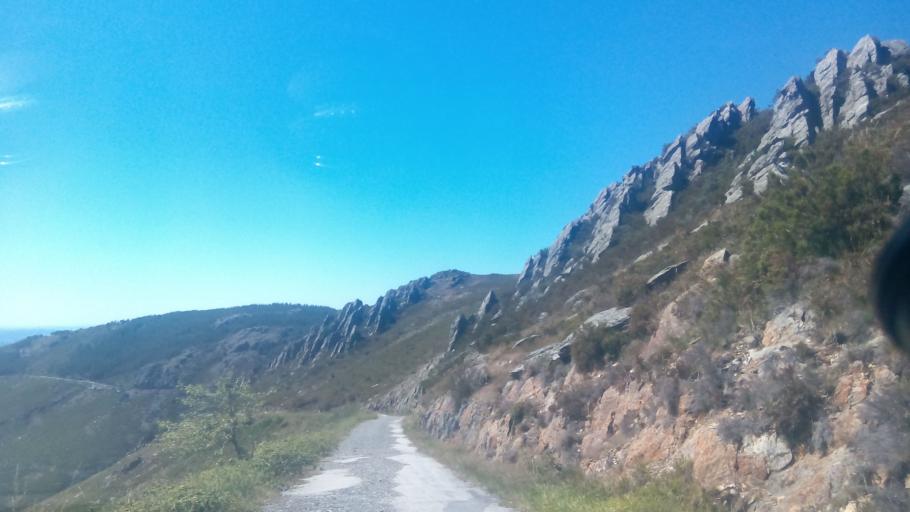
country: PT
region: Vila Real
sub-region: Mesao Frio
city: Mesao Frio
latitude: 41.2661
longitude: -7.9033
